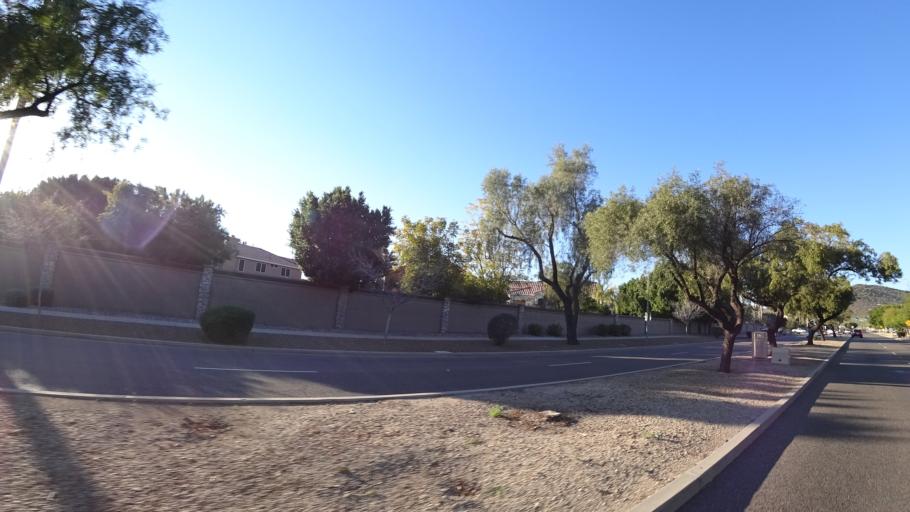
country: US
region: Arizona
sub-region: Maricopa County
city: Peoria
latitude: 33.6811
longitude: -112.1867
